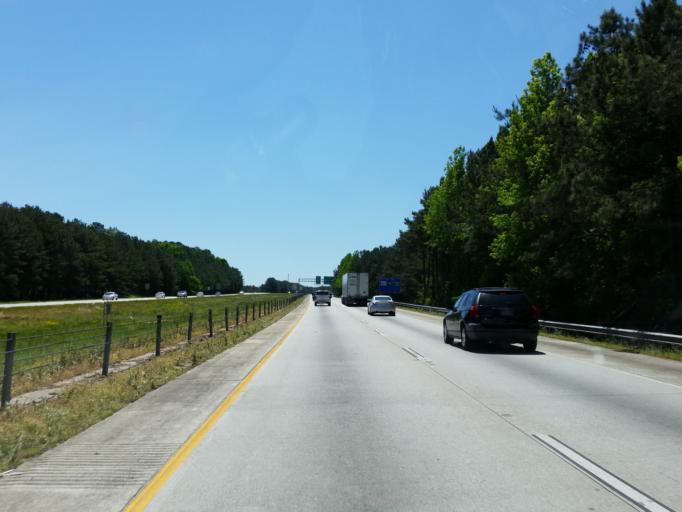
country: US
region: Georgia
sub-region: Henry County
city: Stockbridge
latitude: 33.5616
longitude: -84.2718
